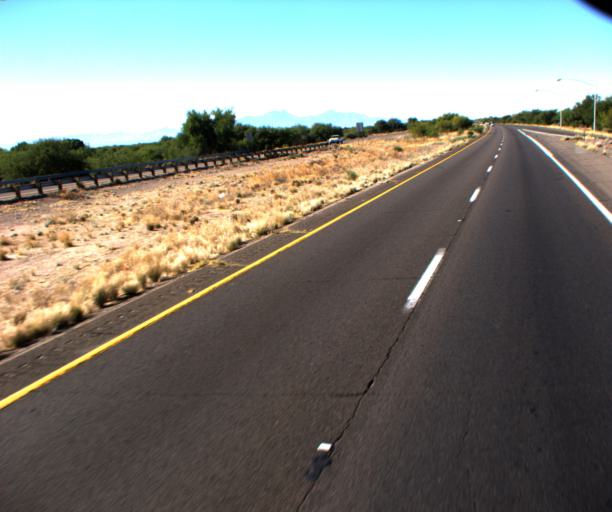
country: US
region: Arizona
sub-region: Pima County
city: Drexel Heights
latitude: 32.1030
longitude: -110.9934
